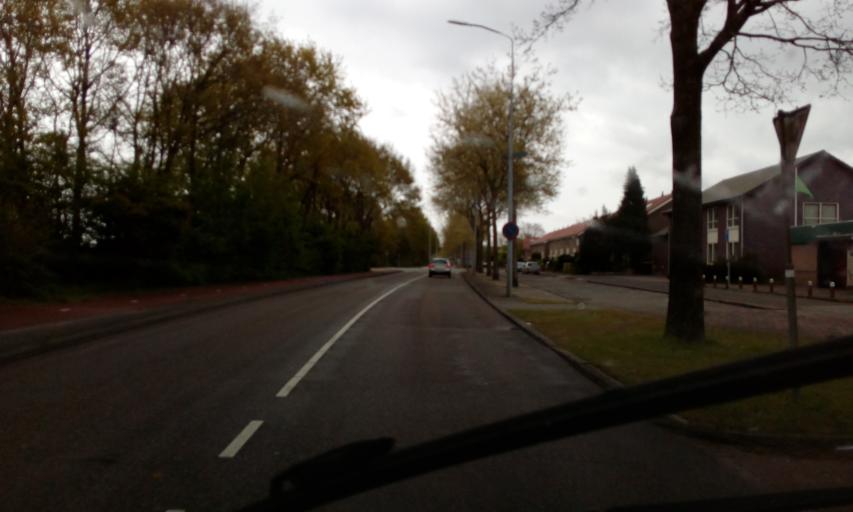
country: NL
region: North Holland
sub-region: Gemeente Huizen
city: Huizen
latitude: 52.3054
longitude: 5.2301
